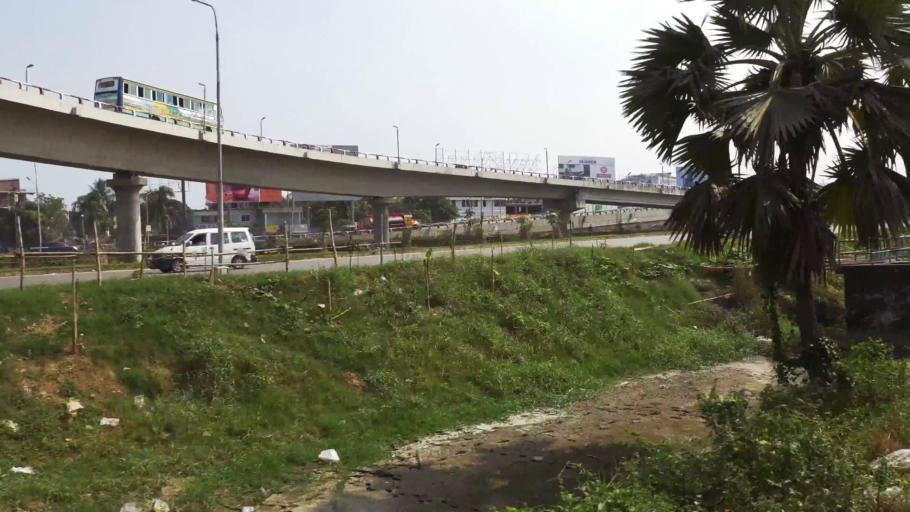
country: BD
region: Dhaka
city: Tungi
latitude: 23.8815
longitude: 90.4064
